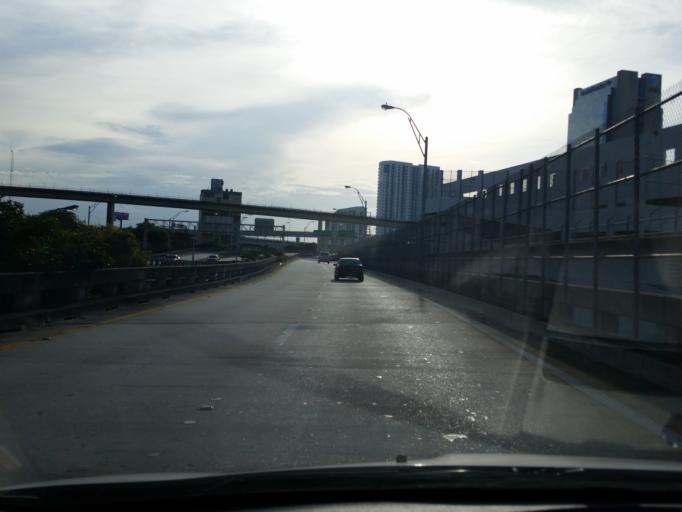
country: US
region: Florida
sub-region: Miami-Dade County
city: Miami
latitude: 25.7718
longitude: -80.1934
